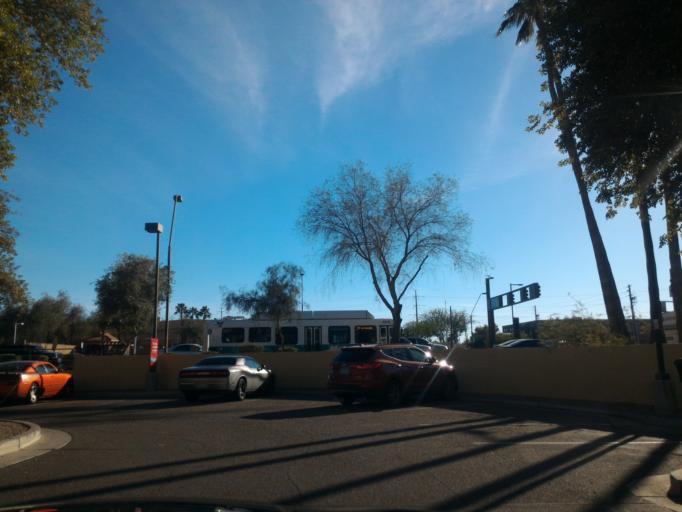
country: US
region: Arizona
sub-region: Maricopa County
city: Guadalupe
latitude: 33.3788
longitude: -111.9627
